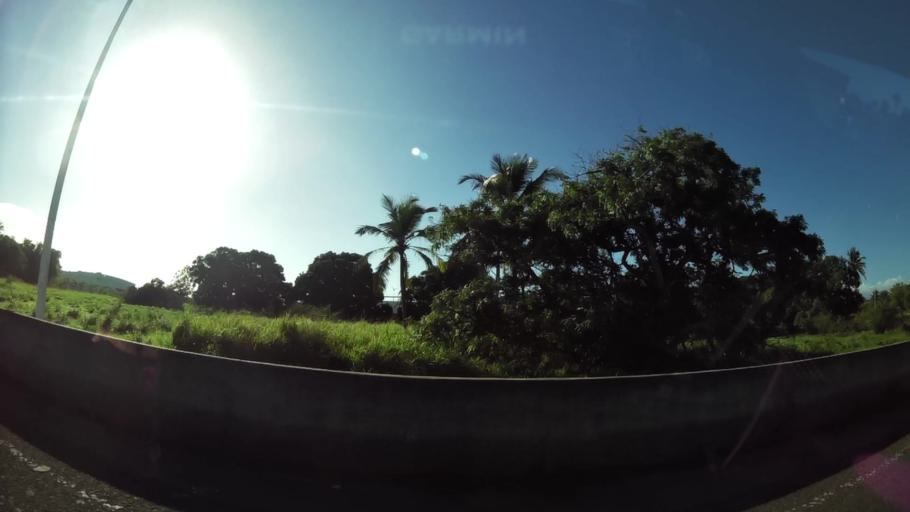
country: GP
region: Guadeloupe
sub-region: Guadeloupe
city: Les Abymes
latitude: 16.2738
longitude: -61.5231
